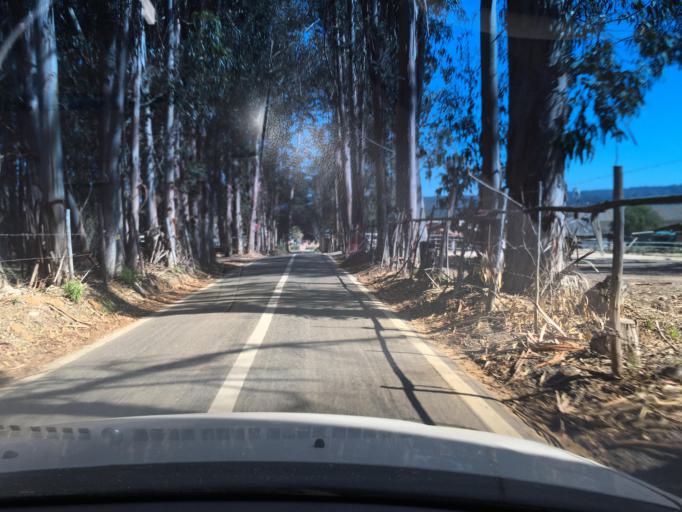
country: CL
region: Valparaiso
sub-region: San Antonio Province
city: El Tabo
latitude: -33.4167
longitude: -71.6212
